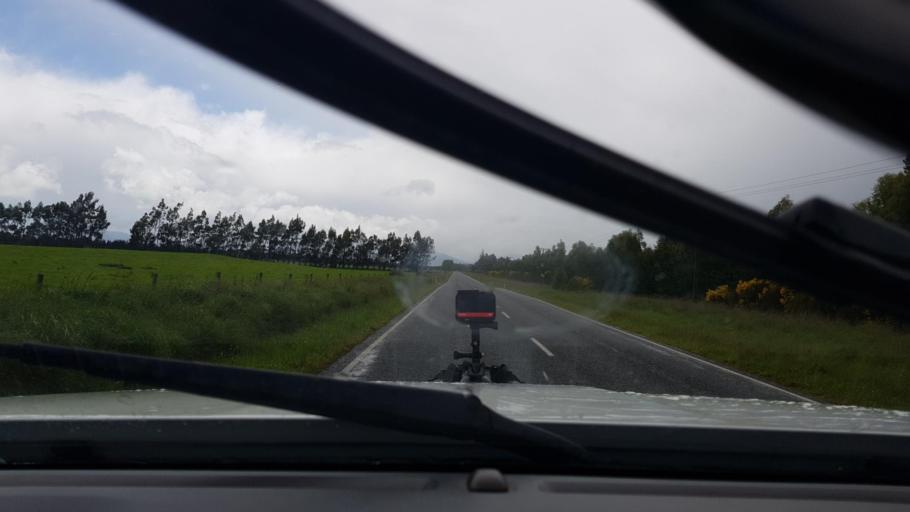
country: NZ
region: Southland
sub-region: Southland District
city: Winton
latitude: -45.7394
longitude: 168.3961
